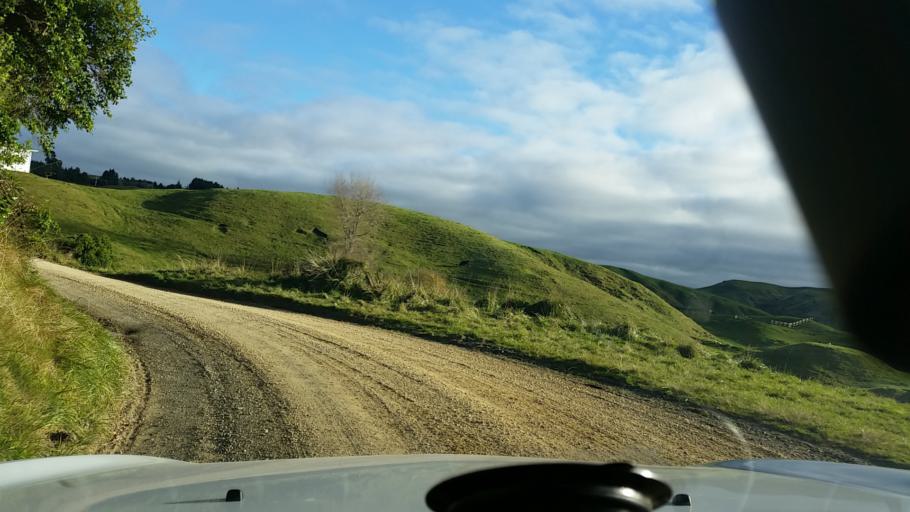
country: NZ
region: Hawke's Bay
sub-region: Napier City
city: Napier
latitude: -39.2599
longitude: 176.8482
